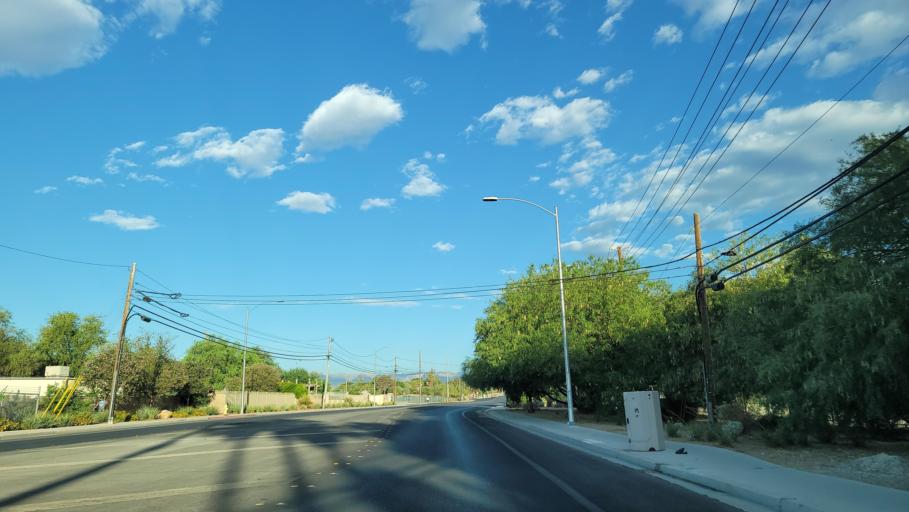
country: US
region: Nevada
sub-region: Clark County
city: Las Vegas
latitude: 36.1663
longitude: -115.1881
